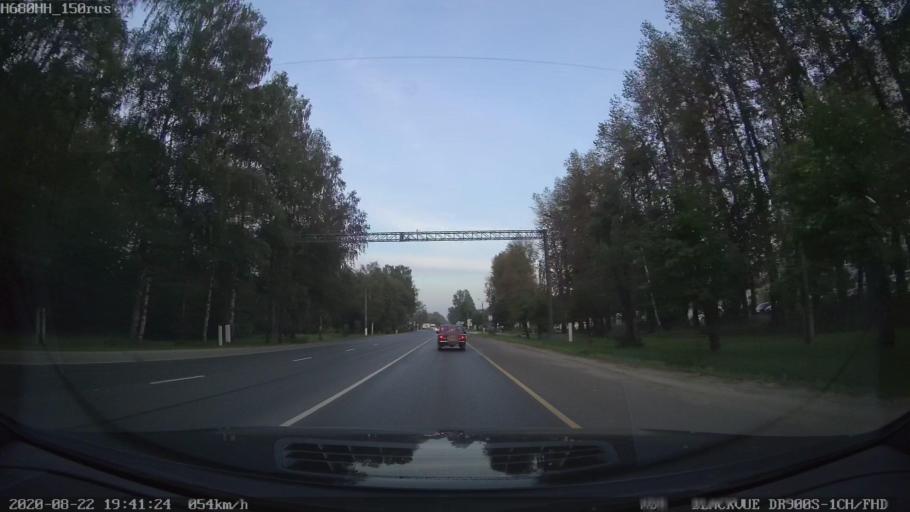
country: RU
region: Tverskaya
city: Emmaus
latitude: 56.8027
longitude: 36.0309
